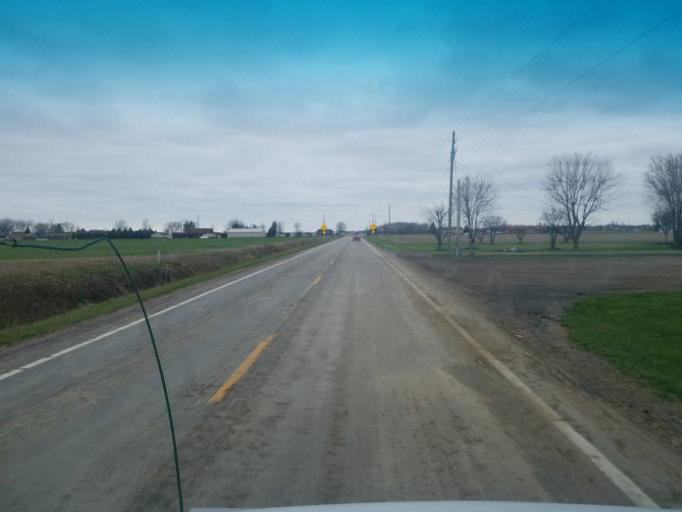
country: US
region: Ohio
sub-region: Allen County
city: Delphos
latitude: 40.9144
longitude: -84.3507
